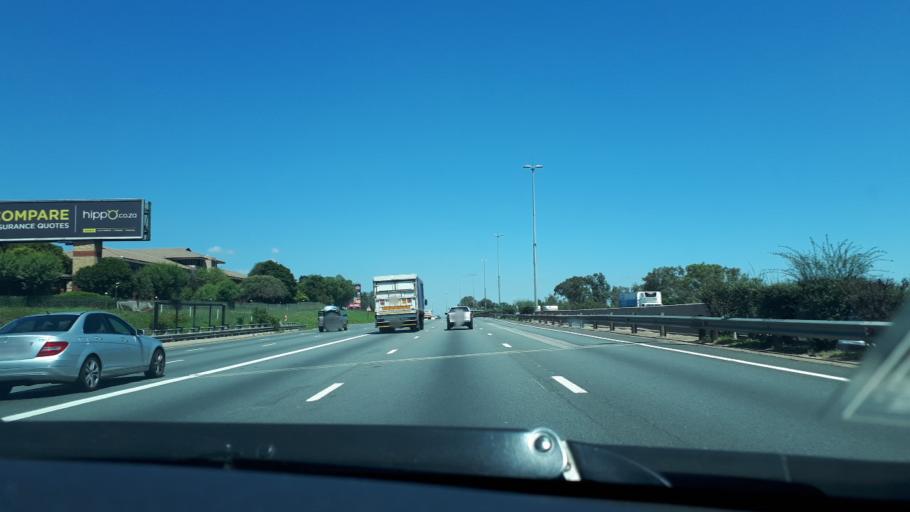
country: ZA
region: Gauteng
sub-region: City of Johannesburg Metropolitan Municipality
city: Midrand
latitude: -26.0445
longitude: 28.0909
